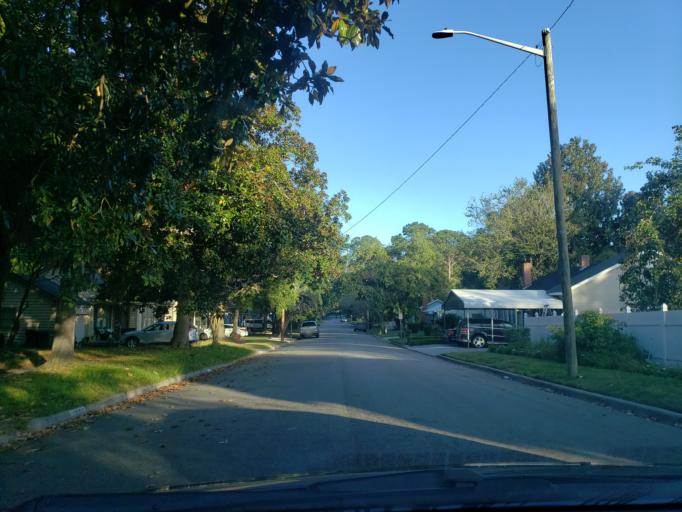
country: US
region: Georgia
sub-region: Chatham County
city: Savannah
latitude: 32.0534
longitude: -81.0810
